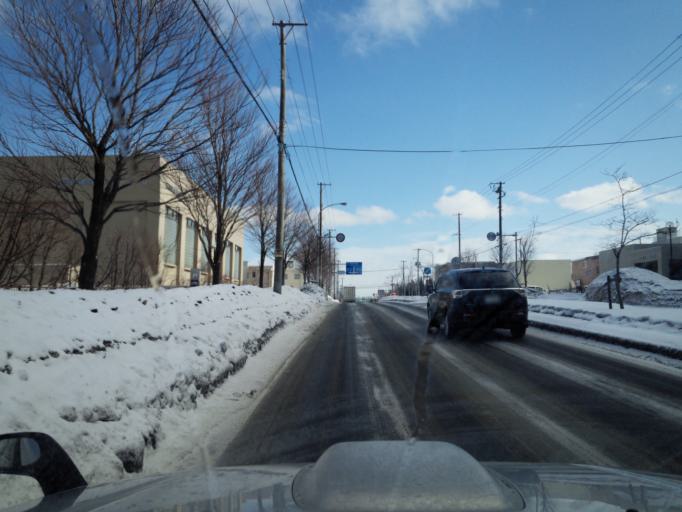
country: JP
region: Hokkaido
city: Kitahiroshima
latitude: 42.9906
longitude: 141.4520
